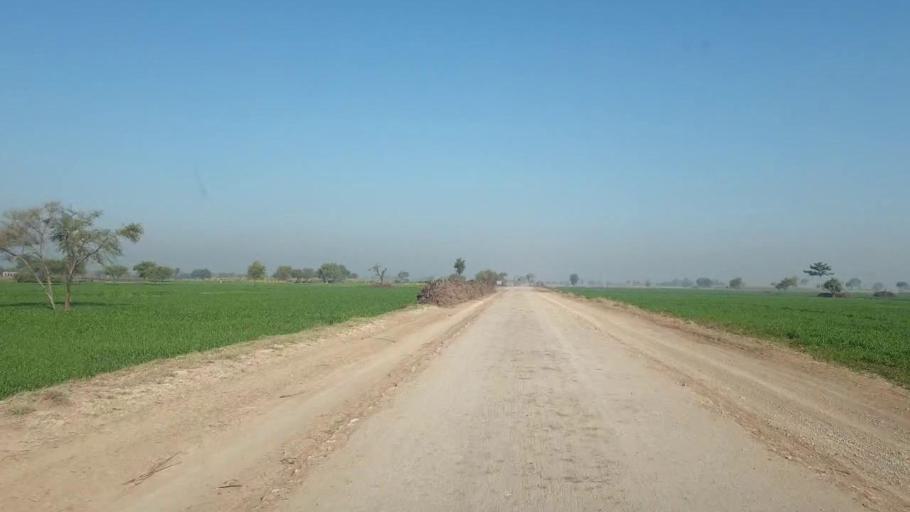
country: PK
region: Sindh
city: Shahdadpur
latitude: 25.9407
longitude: 68.5035
